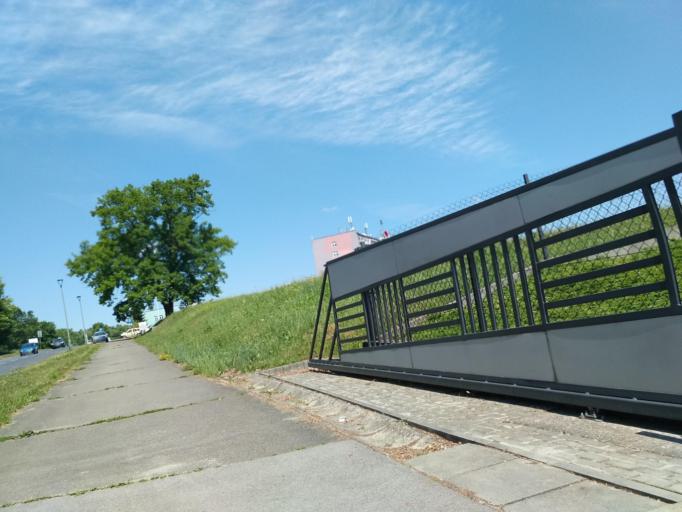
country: PL
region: Subcarpathian Voivodeship
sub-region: Krosno
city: Krosno
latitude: 49.6995
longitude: 21.7832
